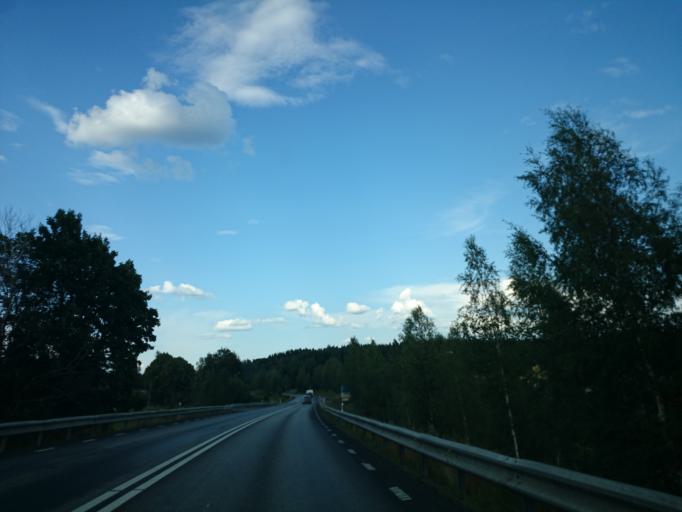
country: SE
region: OErebro
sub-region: Lindesbergs Kommun
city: Lindesberg
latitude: 59.6377
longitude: 15.2221
